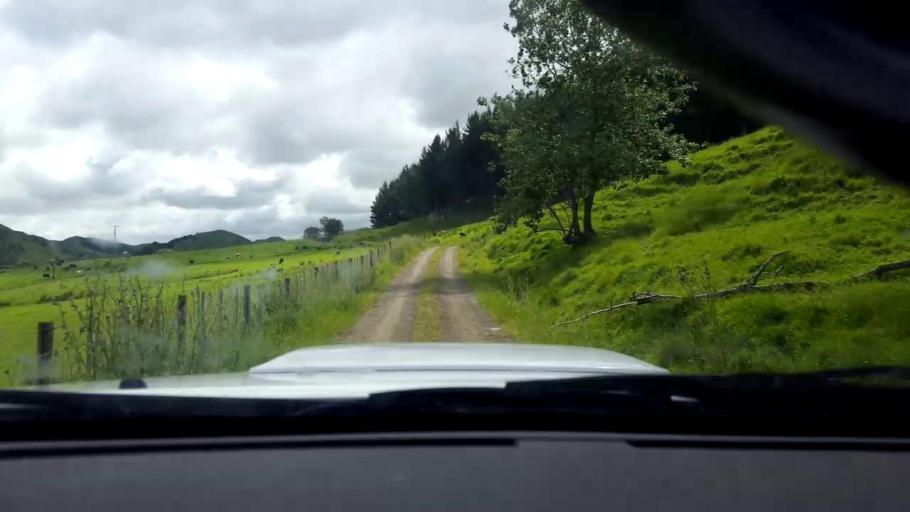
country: NZ
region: Gisborne
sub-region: Gisborne District
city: Gisborne
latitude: -38.4907
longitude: 177.6775
